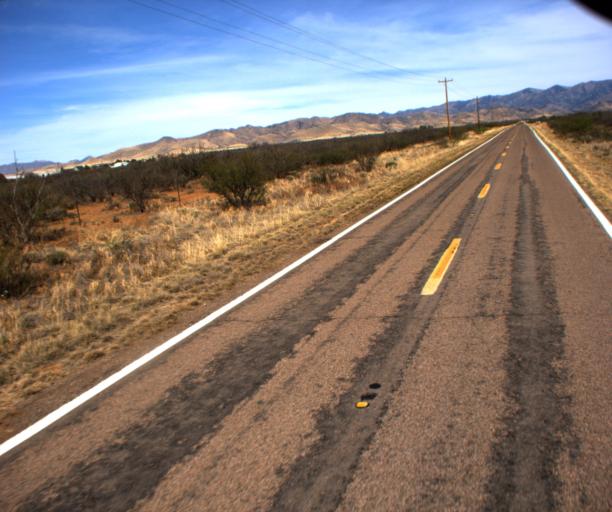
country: US
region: Arizona
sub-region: Cochise County
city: Willcox
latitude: 31.8760
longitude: -109.5242
